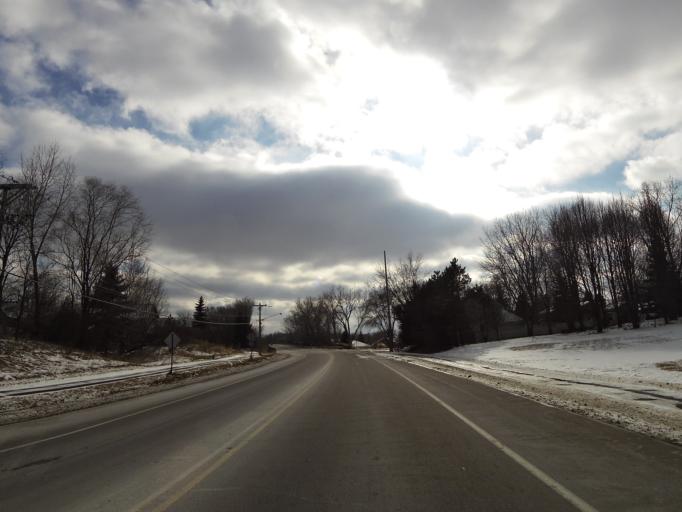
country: US
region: Minnesota
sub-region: Hennepin County
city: Eden Prairie
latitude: 44.8806
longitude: -93.4847
